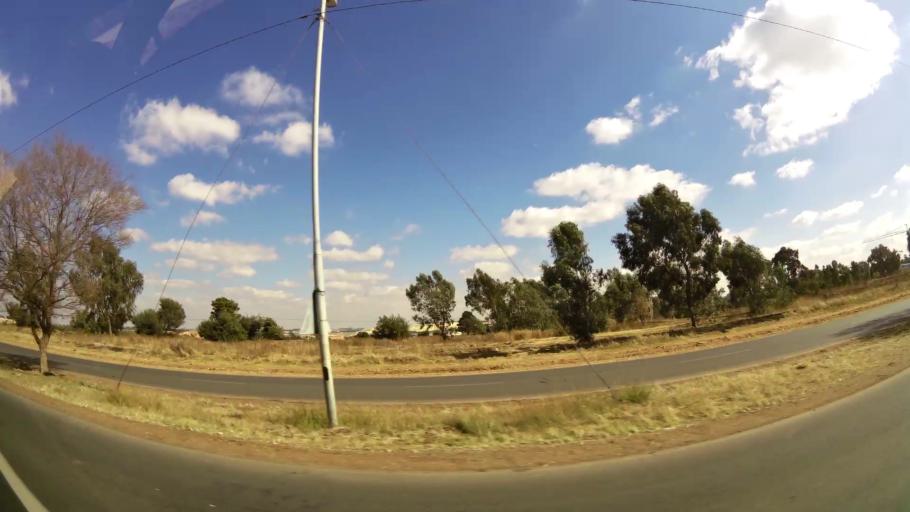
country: ZA
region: Gauteng
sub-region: West Rand District Municipality
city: Krugersdorp
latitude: -26.1294
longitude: 27.8018
